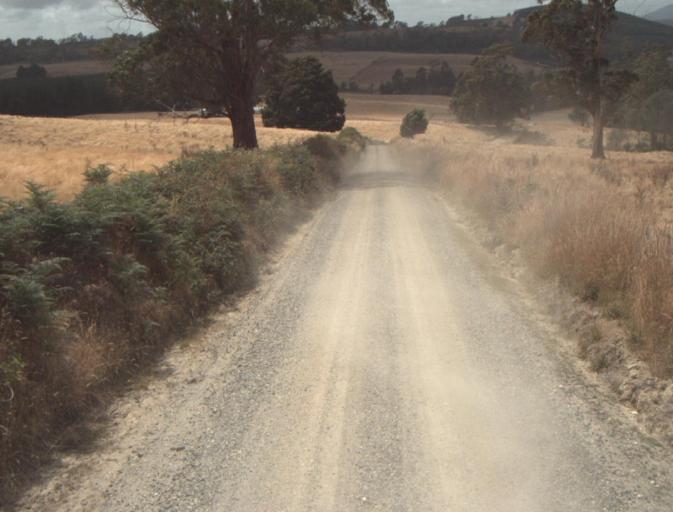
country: AU
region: Tasmania
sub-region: Launceston
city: Mayfield
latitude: -41.1715
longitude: 147.2011
